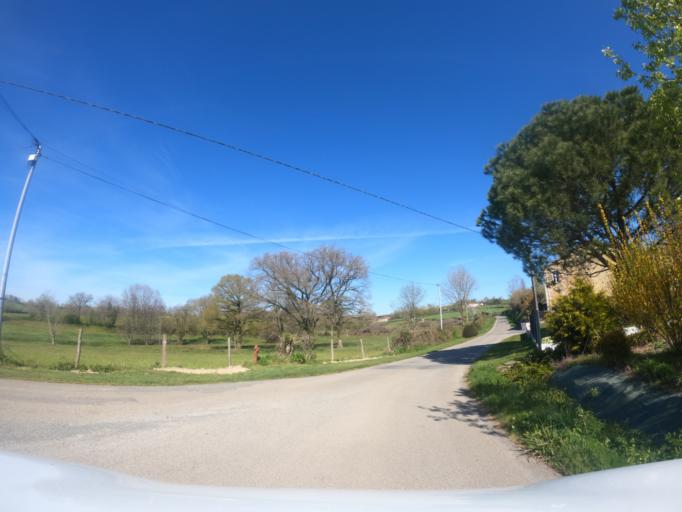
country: FR
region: Pays de la Loire
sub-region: Departement de la Vendee
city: Saint-Pierre-du-Chemin
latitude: 46.6716
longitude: -0.6976
